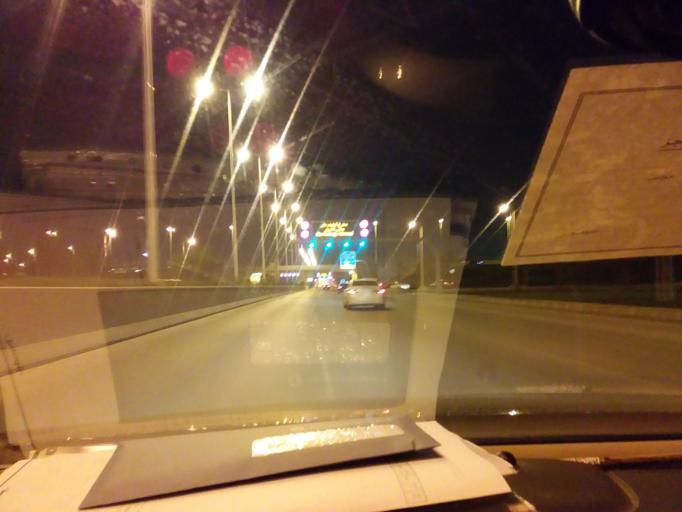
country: SA
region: Ar Riyad
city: Riyadh
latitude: 24.7263
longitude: 46.7074
